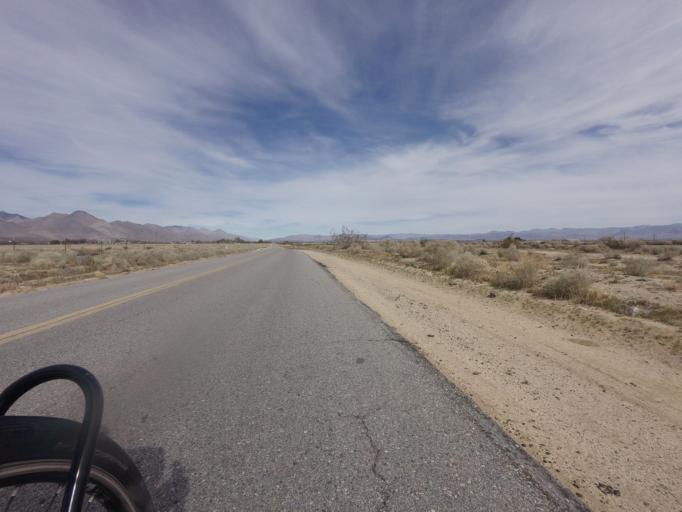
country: US
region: California
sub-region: Kern County
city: Inyokern
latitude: 35.7183
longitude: -117.8335
